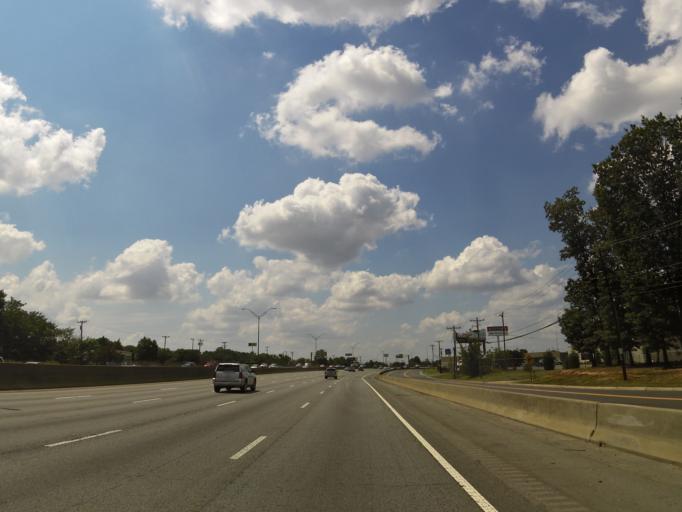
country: US
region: North Carolina
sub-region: Mecklenburg County
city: Charlotte
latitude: 35.2772
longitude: -80.8005
